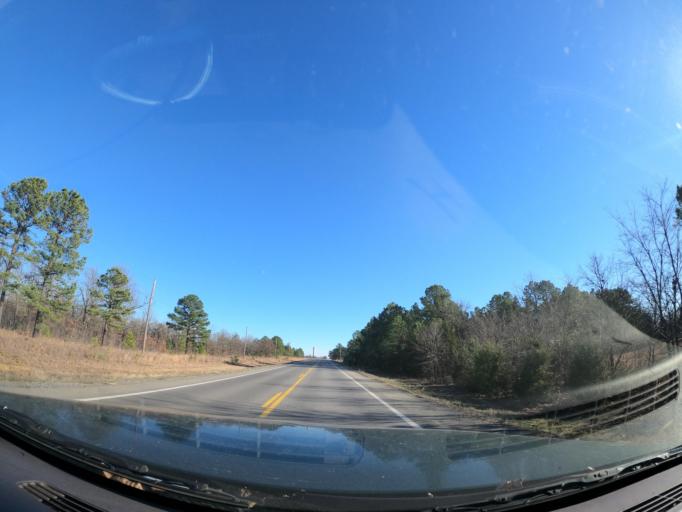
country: US
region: Oklahoma
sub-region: Pittsburg County
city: Longtown
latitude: 35.2319
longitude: -95.4572
